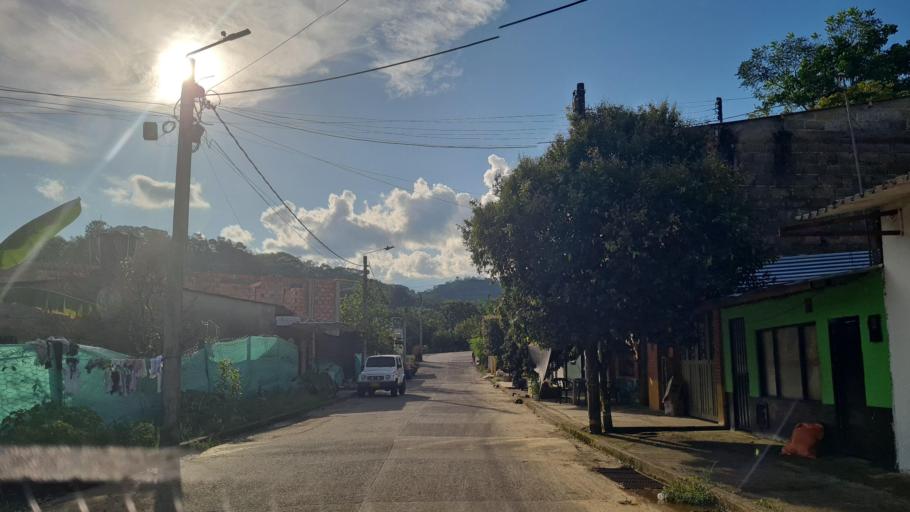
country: CO
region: Boyaca
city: San Luis de Gaceno
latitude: 4.8189
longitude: -73.1699
